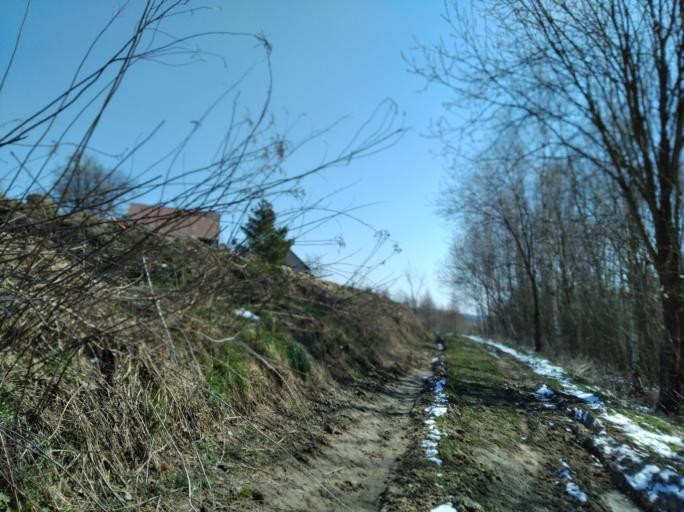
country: PL
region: Subcarpathian Voivodeship
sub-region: Powiat strzyzowski
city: Strzyzow
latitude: 49.8508
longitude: 21.8240
